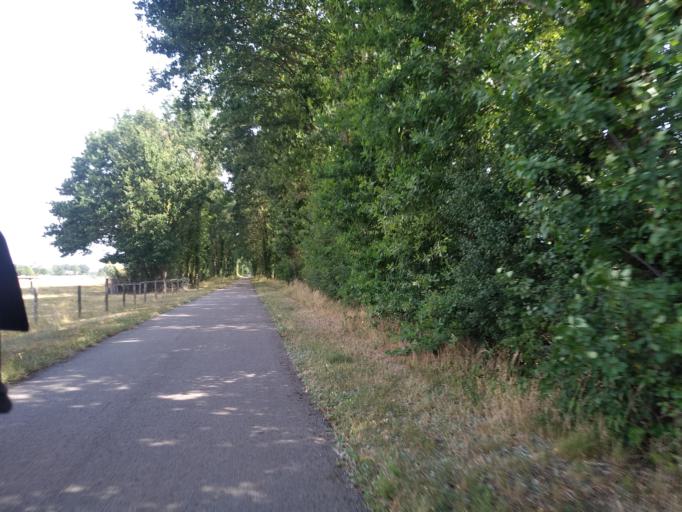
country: FR
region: Bourgogne
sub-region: Departement de Saone-et-Loire
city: Marcigny
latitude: 46.3416
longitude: 4.0283
